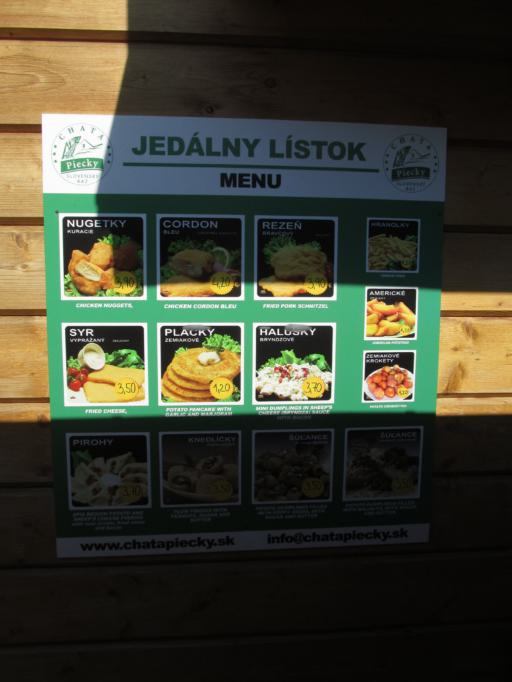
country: SK
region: Kosicky
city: Dobsina
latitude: 48.9451
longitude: 20.3475
